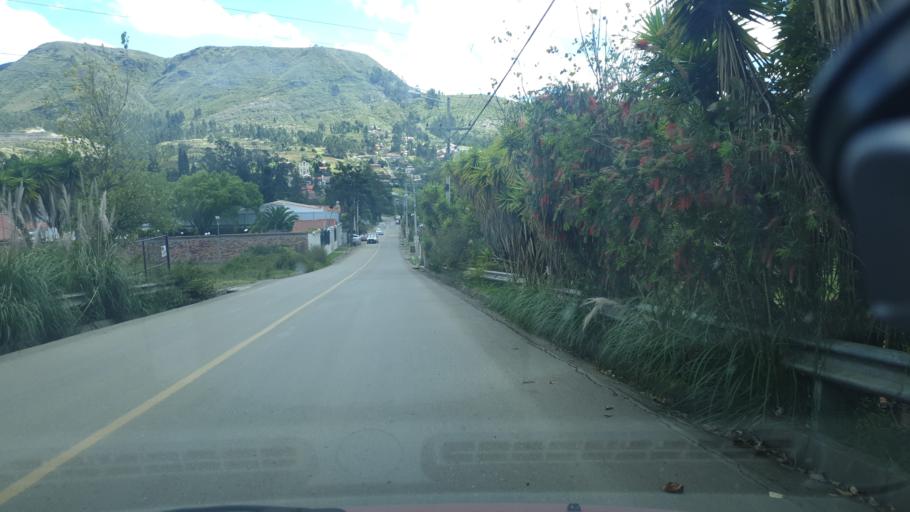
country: EC
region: Azuay
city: Llacao
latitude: -2.8526
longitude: -78.9104
